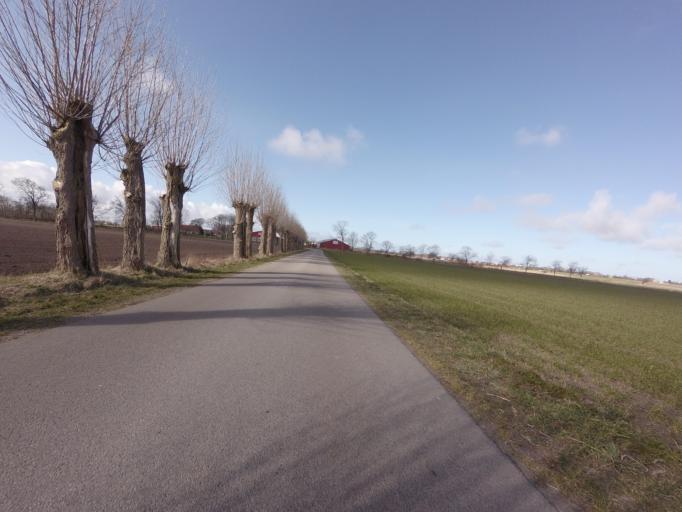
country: SE
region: Skane
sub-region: Hoganas Kommun
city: Hoganas
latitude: 56.1874
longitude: 12.6221
